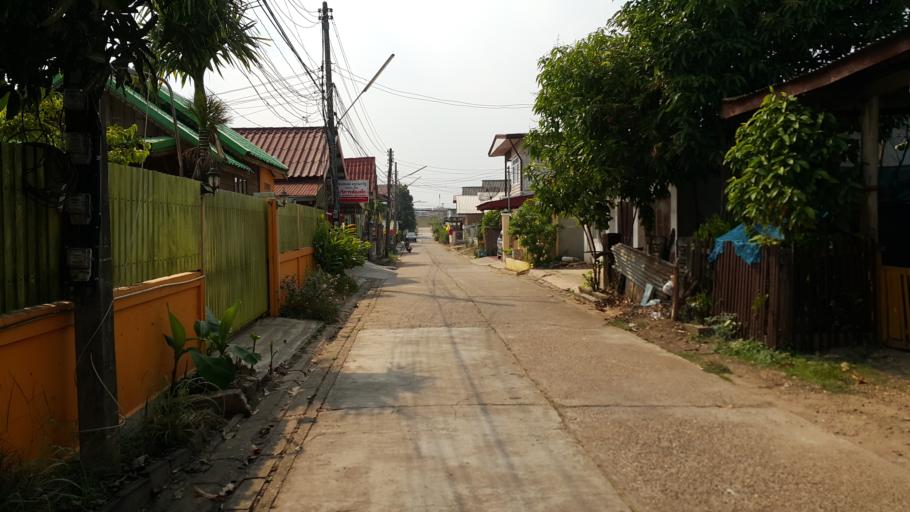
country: TH
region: Nakhon Phanom
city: That Phanom
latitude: 16.9462
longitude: 104.7296
